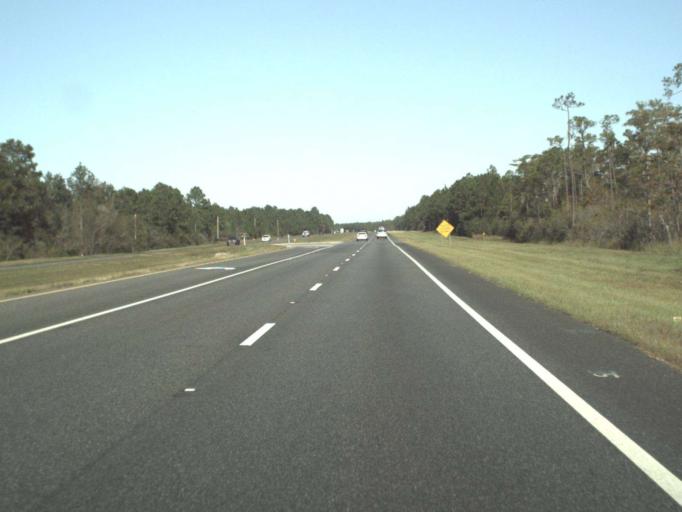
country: US
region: Florida
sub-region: Walton County
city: Seaside
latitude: 30.3207
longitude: -86.0461
